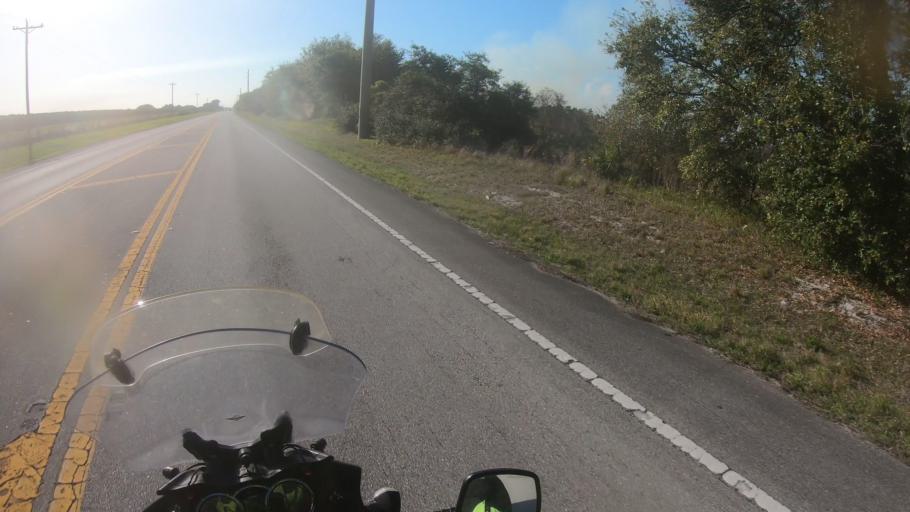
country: US
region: Florida
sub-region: Highlands County
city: Placid Lakes
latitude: 27.2078
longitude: -81.3982
